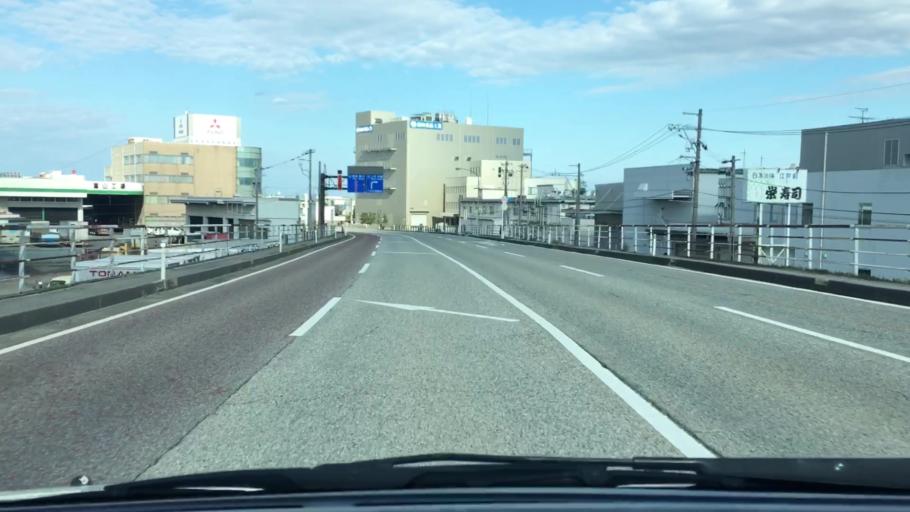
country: JP
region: Toyama
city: Toyama-shi
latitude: 36.6994
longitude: 137.2580
